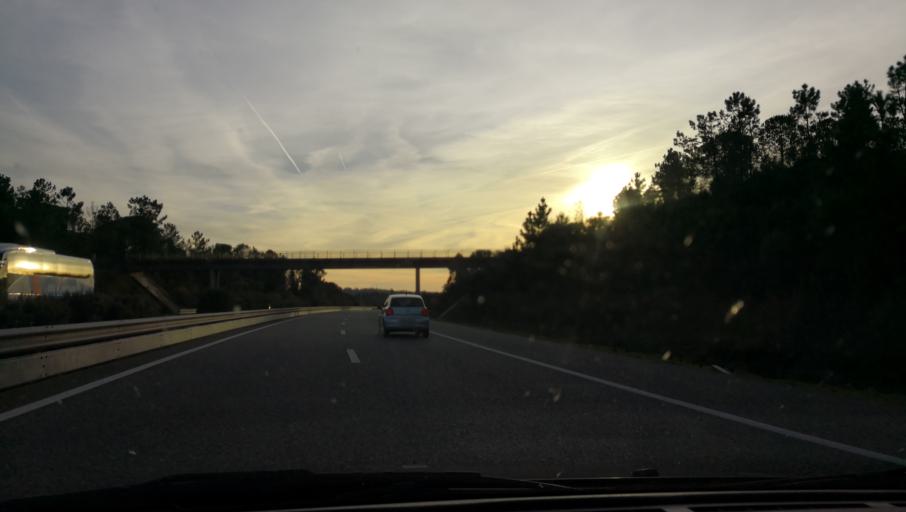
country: PT
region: Coimbra
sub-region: Condeixa-A-Nova
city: Condeixa-a-Nova
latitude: 40.0734
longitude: -8.5389
